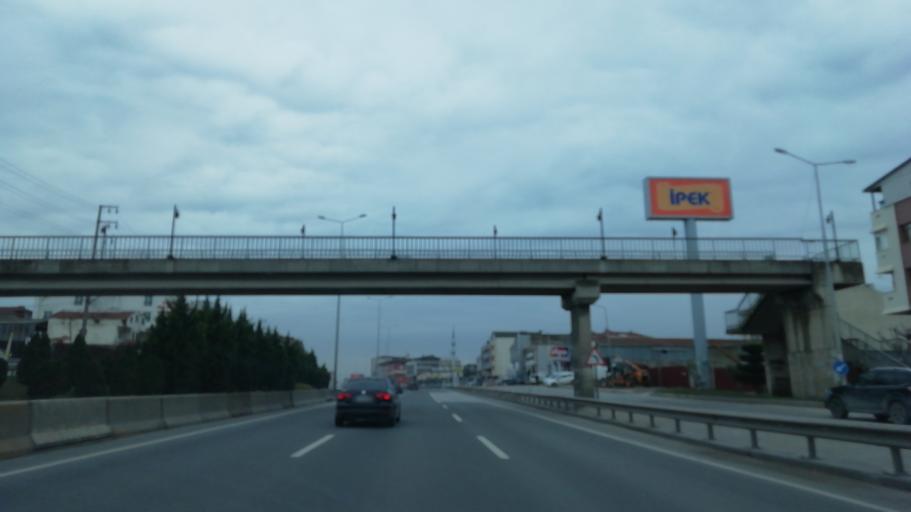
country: TR
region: Kocaeli
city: Korfez
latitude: 40.7596
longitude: 29.7909
